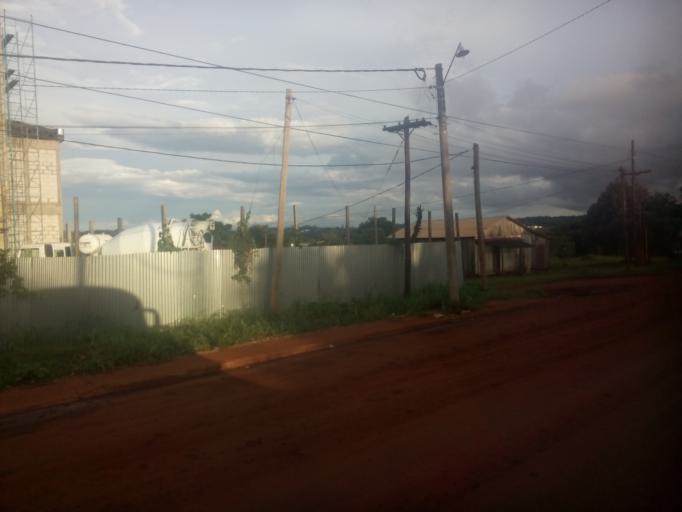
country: AR
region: Misiones
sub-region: Departamento de Obera
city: Obera
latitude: -27.4928
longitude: -55.1448
